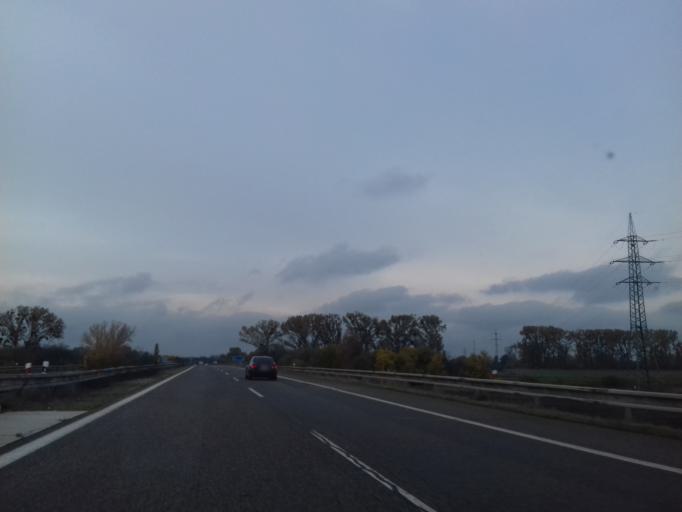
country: CZ
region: South Moravian
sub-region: Okres Breclav
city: Lanzhot
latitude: 48.6332
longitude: 17.0053
